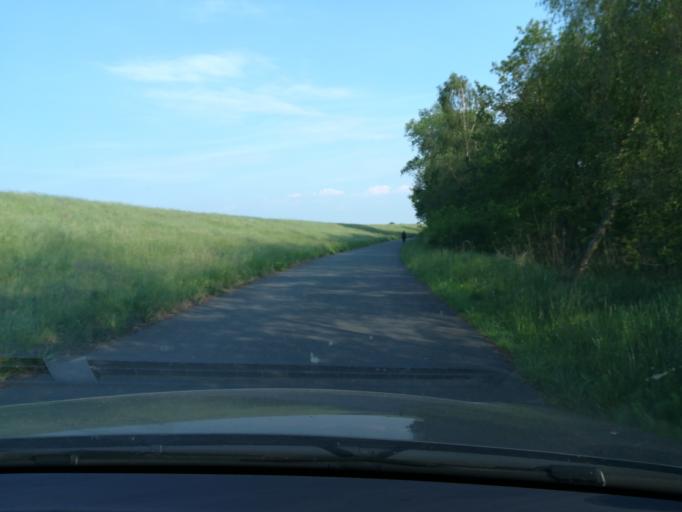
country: DE
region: Lower Saxony
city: Artlenburg
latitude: 53.3825
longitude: 10.4685
